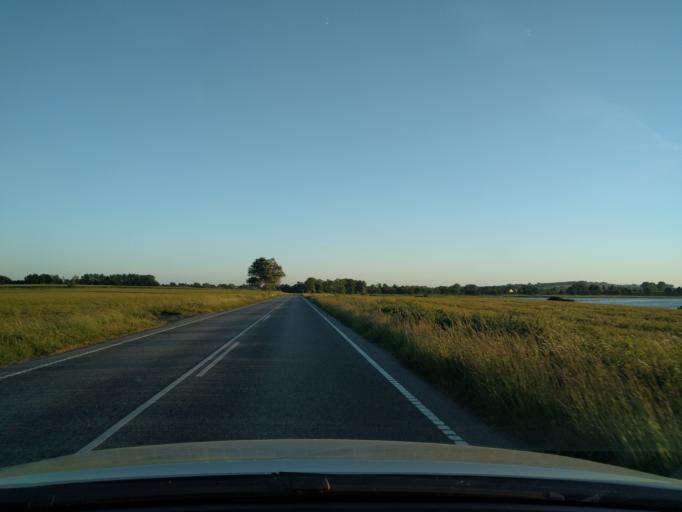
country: DK
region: South Denmark
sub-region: Kerteminde Kommune
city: Kerteminde
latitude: 55.4819
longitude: 10.6181
